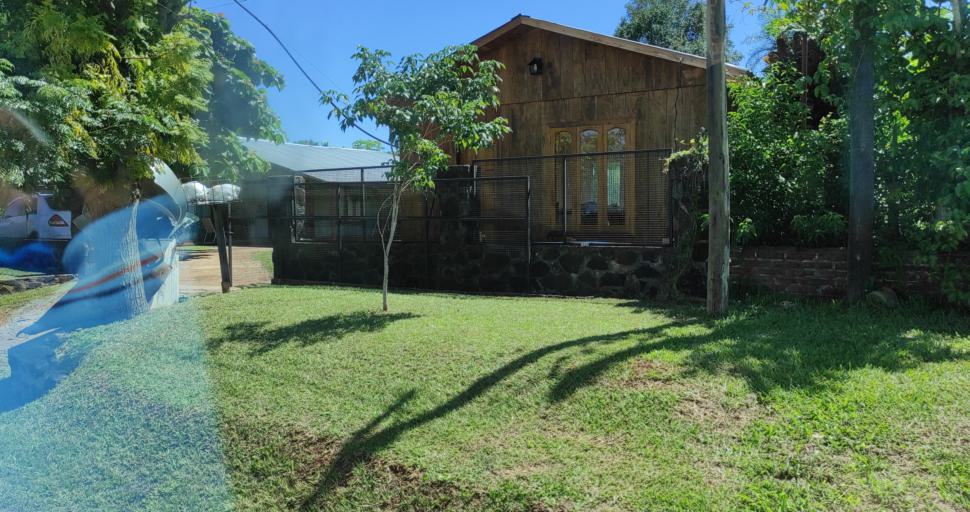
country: AR
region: Misiones
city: El Soberbio
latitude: -27.3017
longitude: -54.1939
